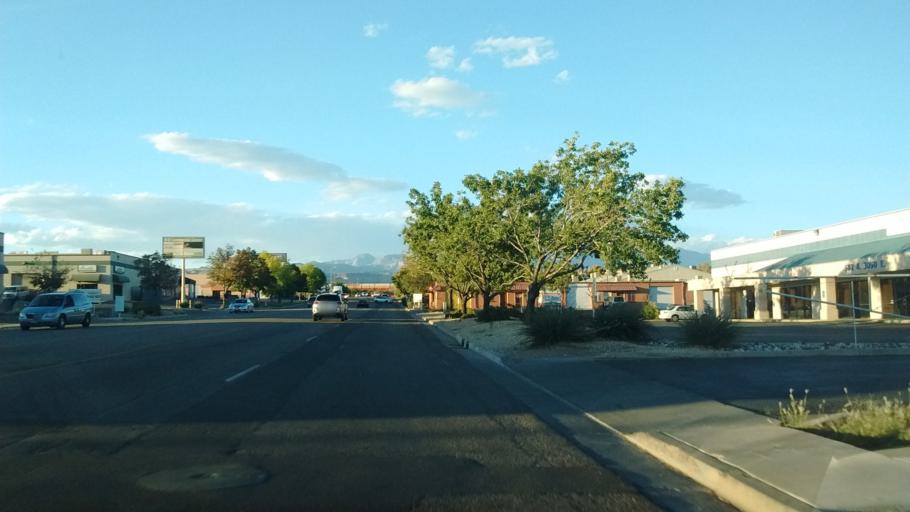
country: US
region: Utah
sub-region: Washington County
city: Washington
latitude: 37.1182
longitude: -113.5207
